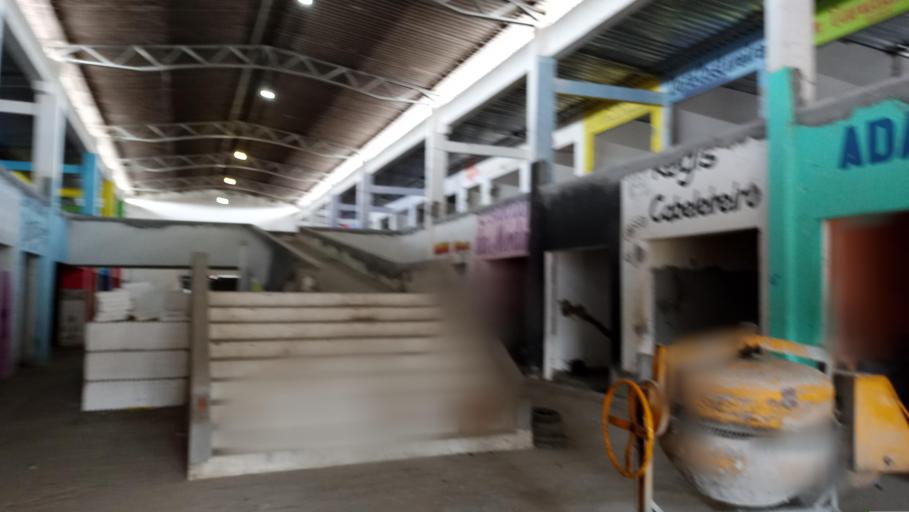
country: BR
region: Bahia
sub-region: Ubata
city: Ubata
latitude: -14.1719
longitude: -39.4643
